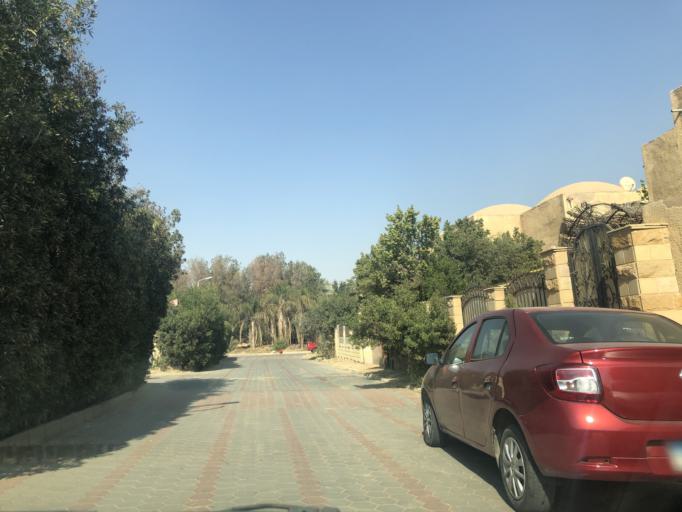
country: EG
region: Al Jizah
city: Madinat Sittah Uktubar
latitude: 29.9562
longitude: 31.0087
